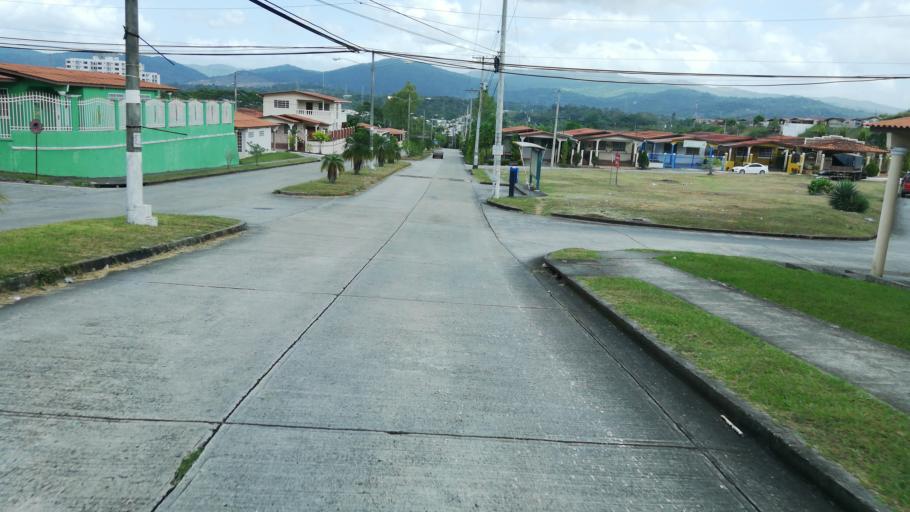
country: PA
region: Panama
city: San Miguelito
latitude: 9.0761
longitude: -79.4577
